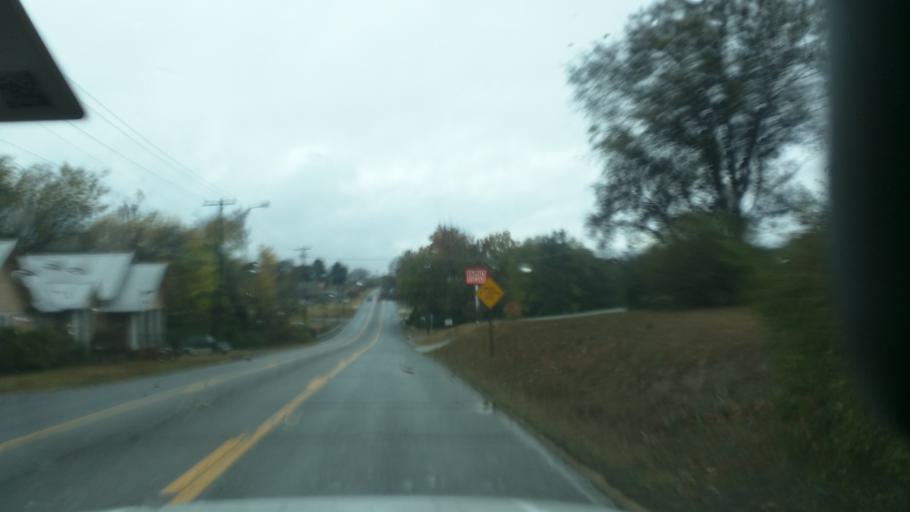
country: US
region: Arkansas
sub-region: Franklin County
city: Ozark
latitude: 35.4878
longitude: -93.8347
